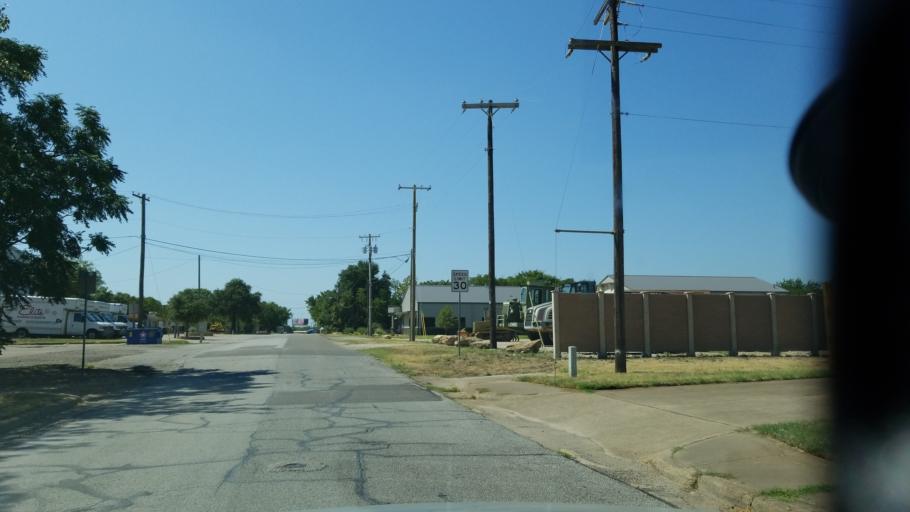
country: US
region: Texas
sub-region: Dallas County
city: Duncanville
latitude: 32.6403
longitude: -96.8991
